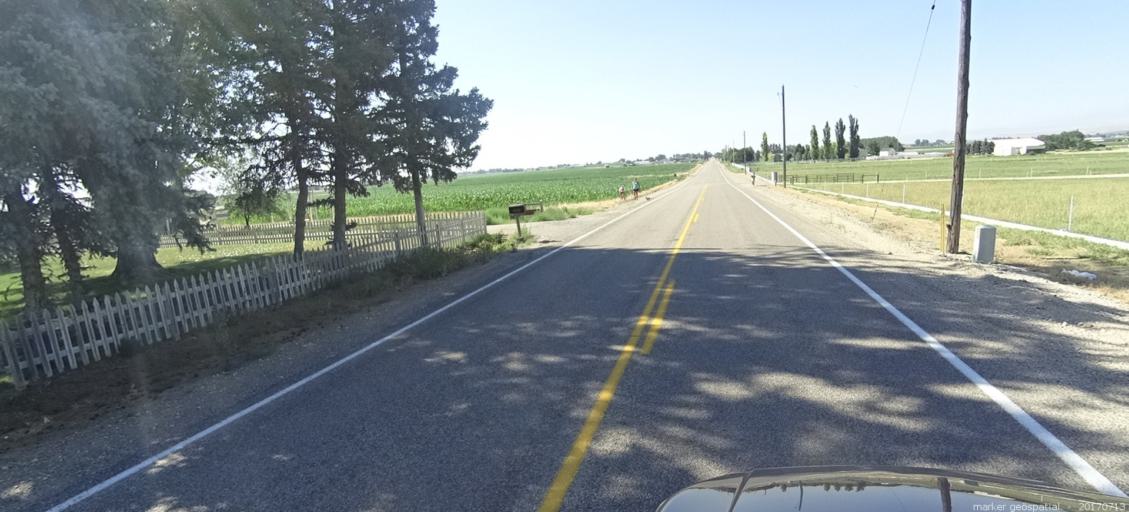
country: US
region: Idaho
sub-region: Ada County
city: Kuna
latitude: 43.5235
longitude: -116.3743
